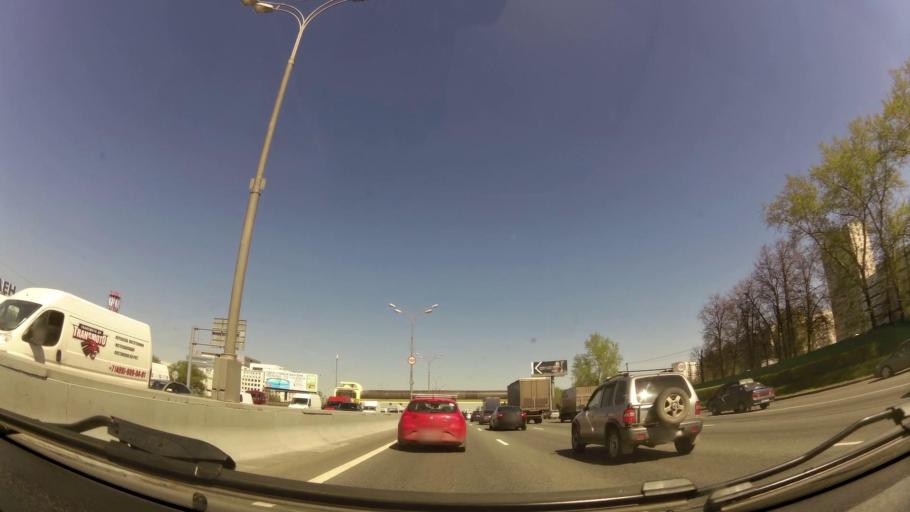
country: RU
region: Moscow
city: Strogino
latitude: 55.8098
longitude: 37.3888
